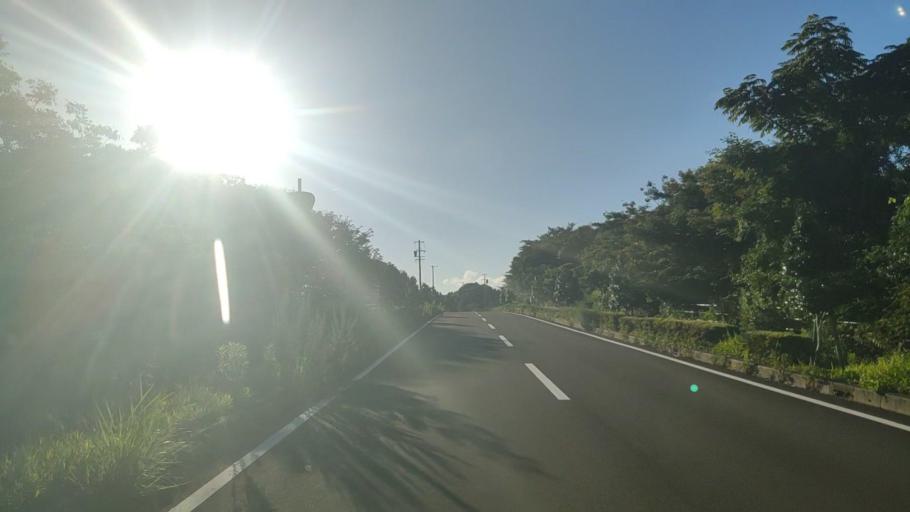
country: JP
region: Mie
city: Toba
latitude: 34.2729
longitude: 136.7798
